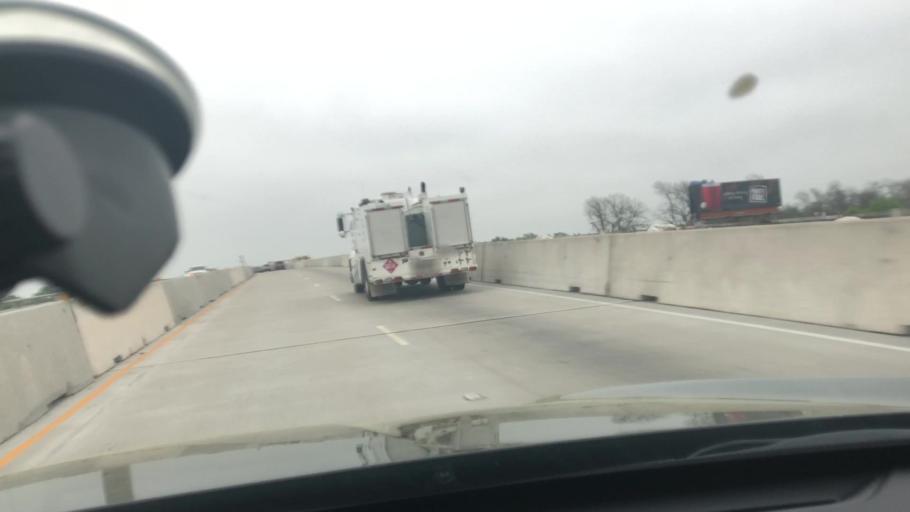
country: US
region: Texas
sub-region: Bell County
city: Temple
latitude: 31.0960
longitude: -97.3694
